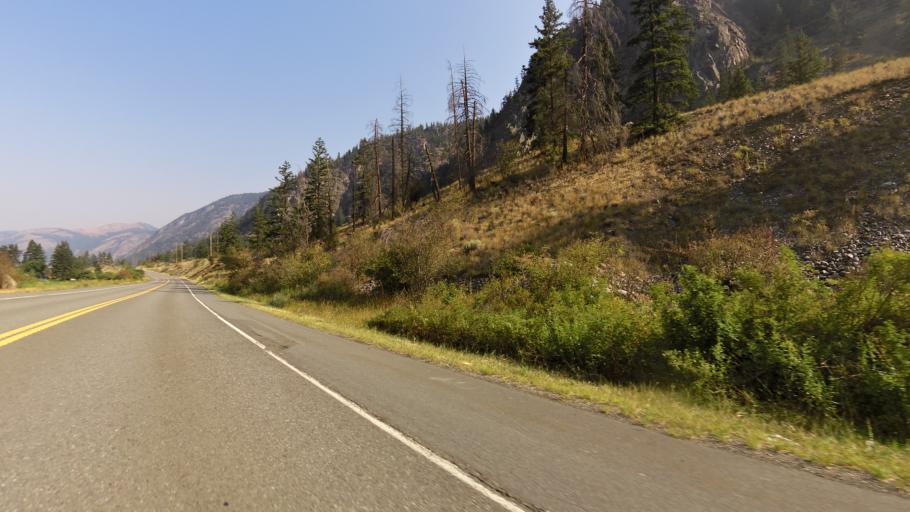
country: CA
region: British Columbia
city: Summerland
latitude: 49.3178
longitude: -120.0370
